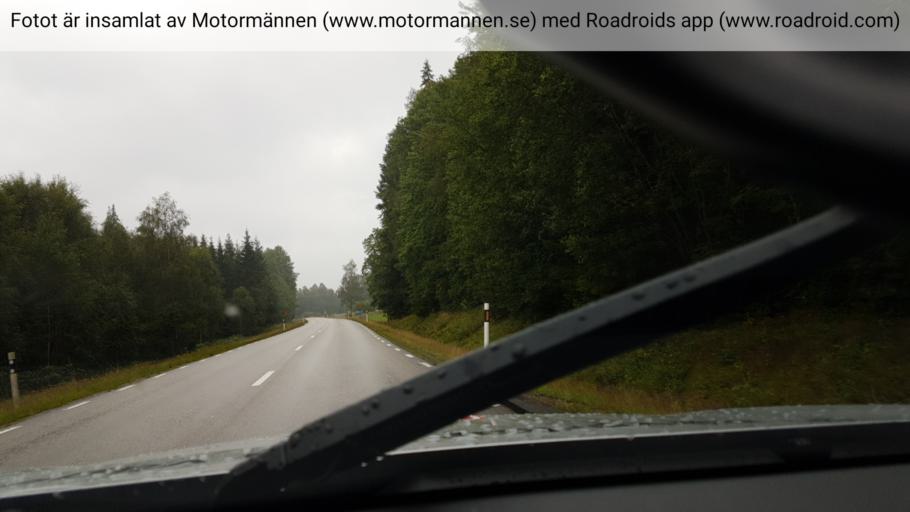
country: SE
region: Vaestra Goetaland
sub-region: Bengtsfors Kommun
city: Dals Langed
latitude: 58.8646
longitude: 12.1894
